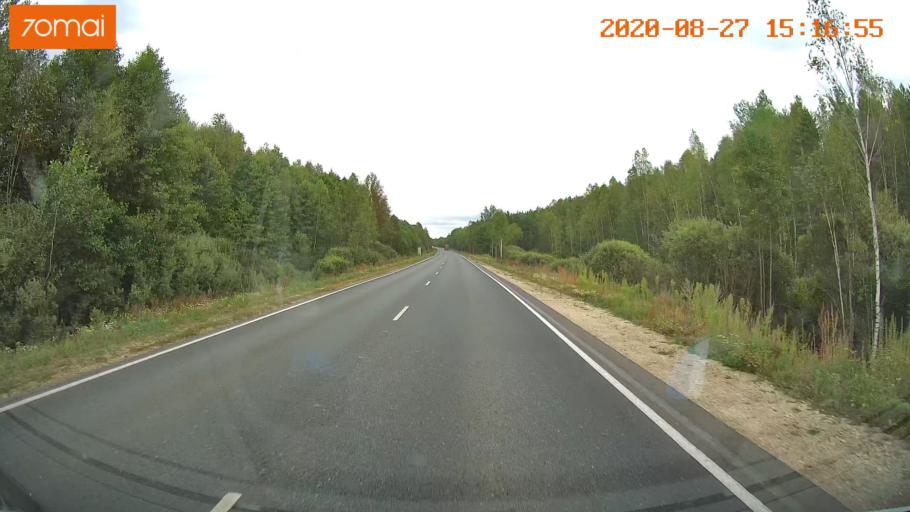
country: RU
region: Vladimir
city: Gus'-Khrustal'nyy
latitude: 55.5724
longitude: 40.6777
